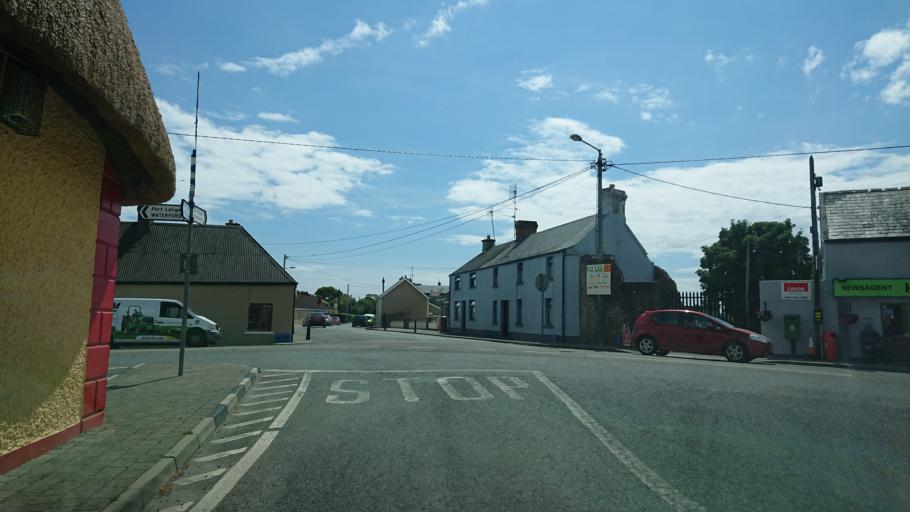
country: IE
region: Munster
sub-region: Waterford
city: Portlaw
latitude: 52.1768
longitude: -7.3355
